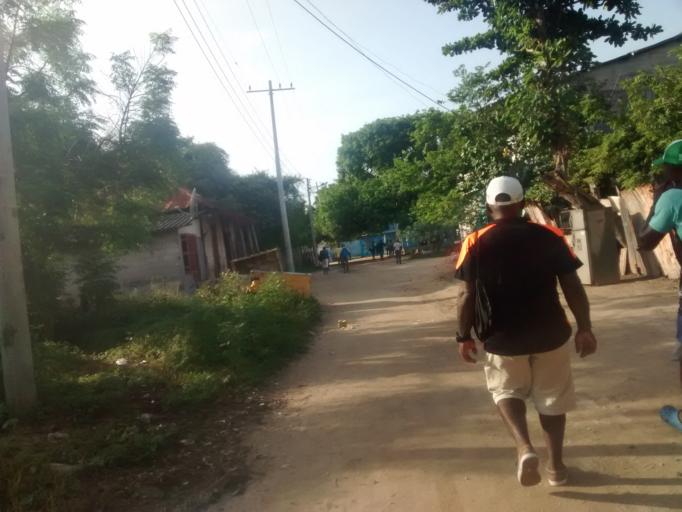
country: CO
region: Bolivar
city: Turbana
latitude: 10.1408
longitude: -75.6862
